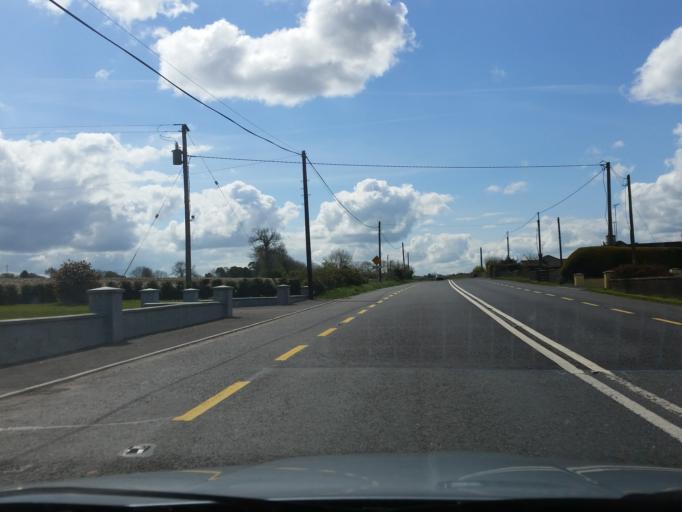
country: IE
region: Leinster
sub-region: An Mhi
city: Slane
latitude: 53.6932
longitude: -6.5393
